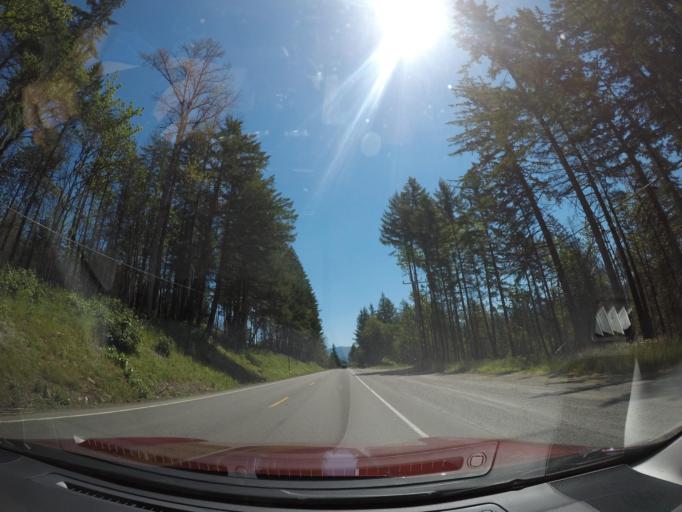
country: US
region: Oregon
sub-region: Linn County
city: Mill City
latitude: 44.7570
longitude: -122.4332
